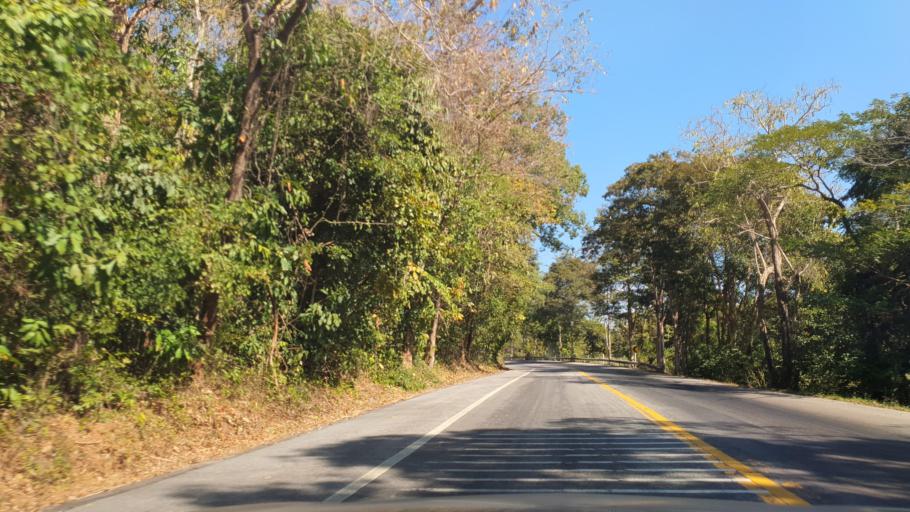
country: TH
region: Kalasin
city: Na Khu
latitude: 16.8492
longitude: 103.9256
